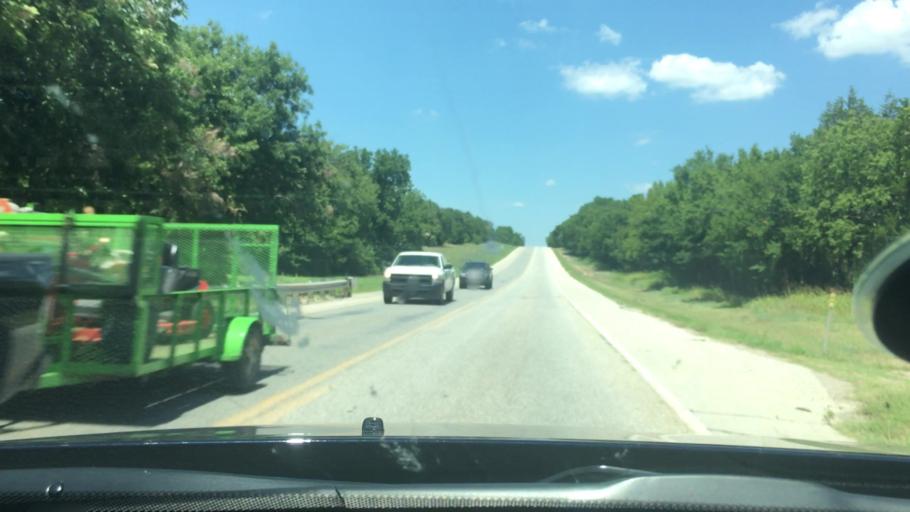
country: US
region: Oklahoma
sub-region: Marshall County
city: Oakland
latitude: 34.1759
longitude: -96.8585
